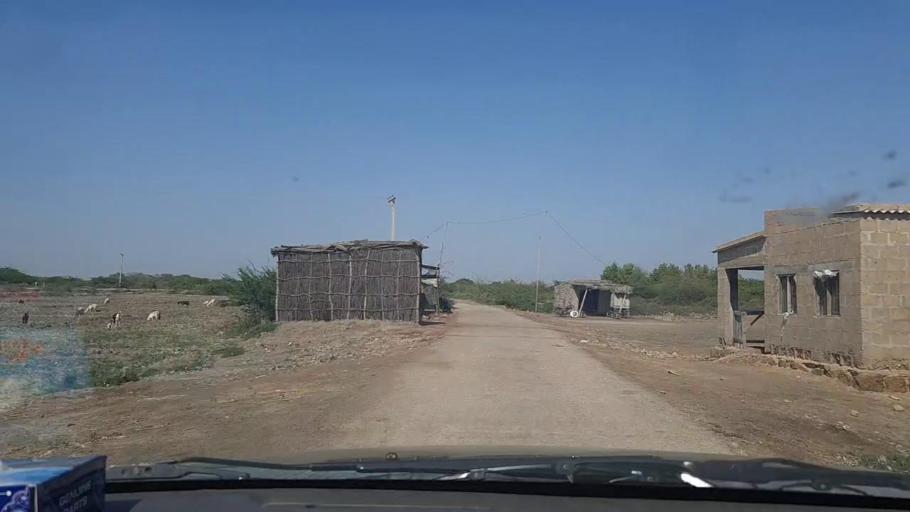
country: PK
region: Sindh
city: Chuhar Jamali
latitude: 24.2927
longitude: 67.7608
